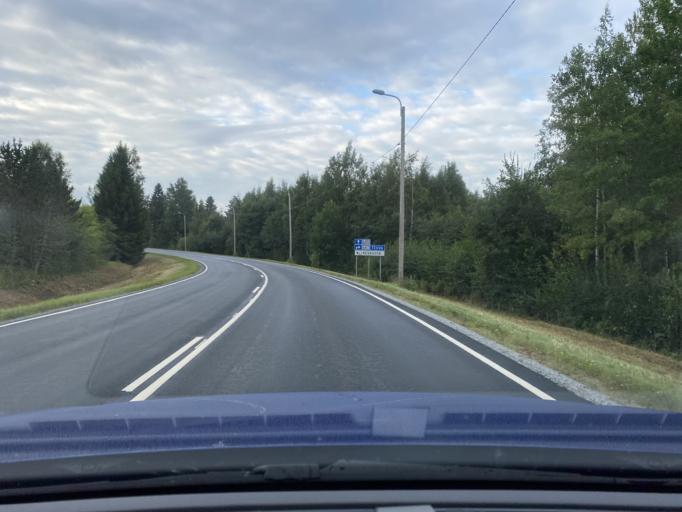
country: FI
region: Southern Ostrobothnia
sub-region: Seinaejoki
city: Jurva
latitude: 62.6845
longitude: 21.9716
